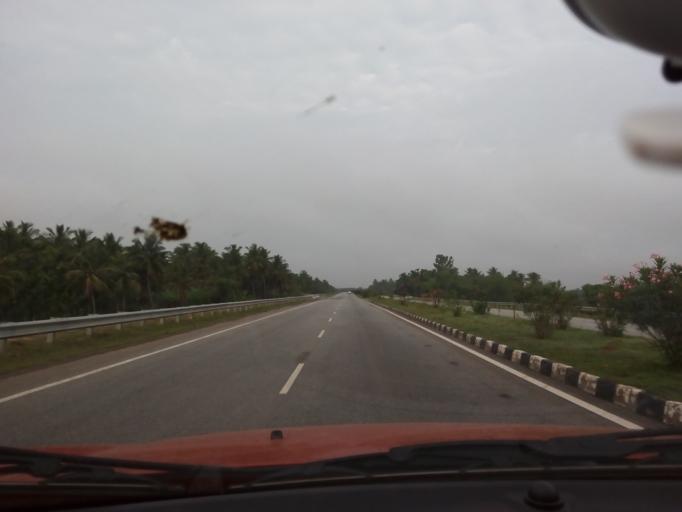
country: IN
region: Karnataka
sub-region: Tumkur
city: Kunigal
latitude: 13.0052
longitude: 76.9898
